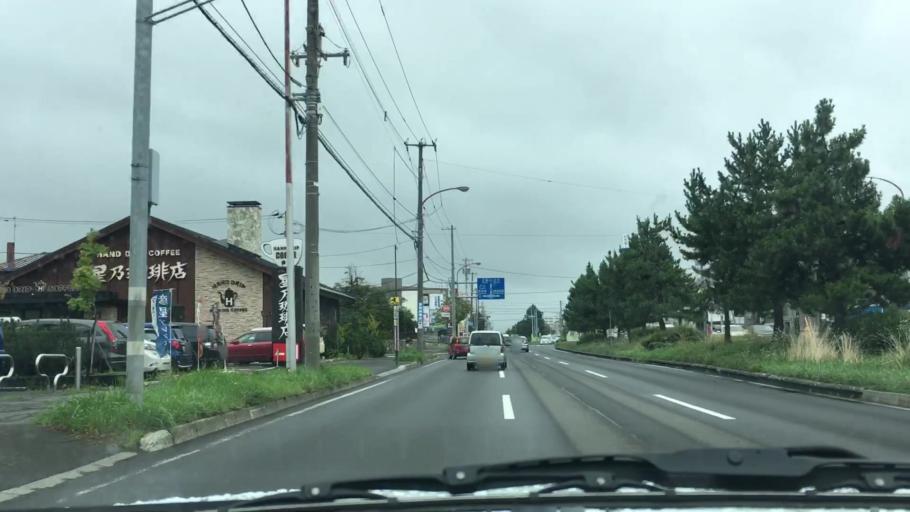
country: JP
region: Hokkaido
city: Sapporo
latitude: 43.0819
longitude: 141.3867
